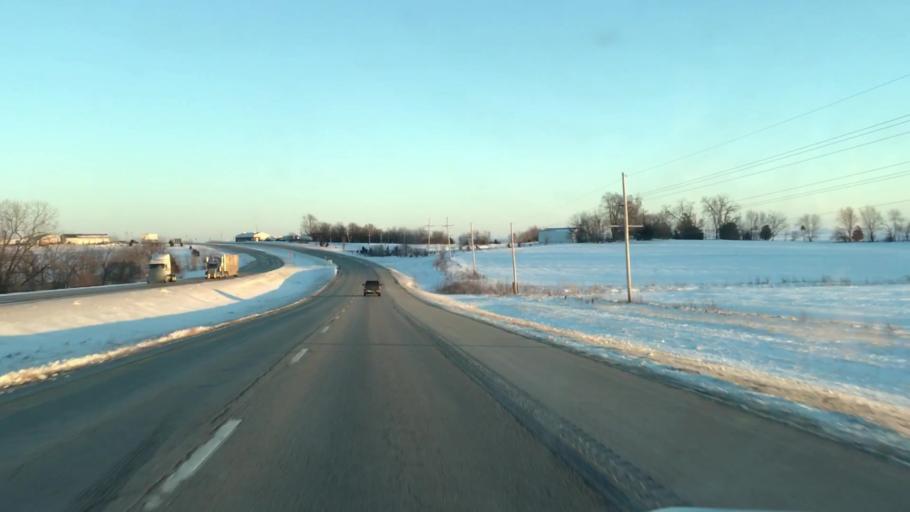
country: US
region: Missouri
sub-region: Clinton County
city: Cameron
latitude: 39.7575
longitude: -94.3446
